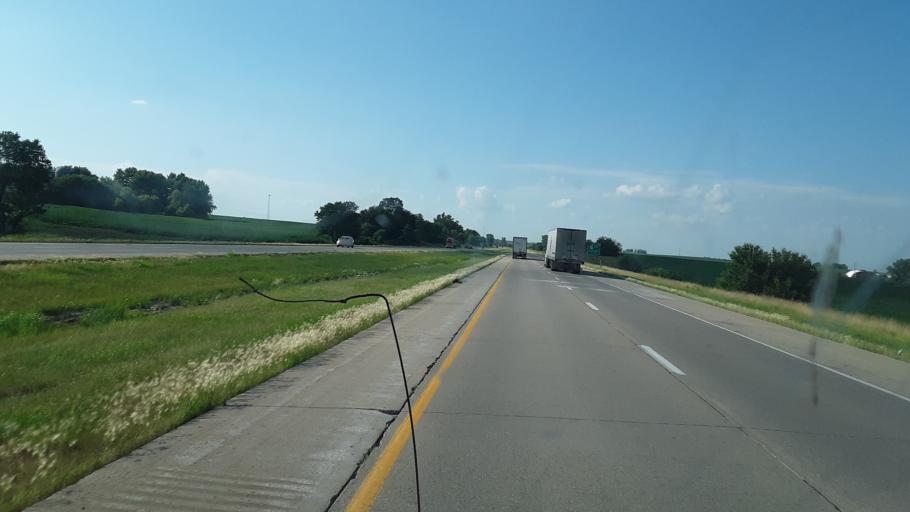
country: US
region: Iowa
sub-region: Black Hawk County
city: Elk Run Heights
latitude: 42.4289
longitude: -92.1868
